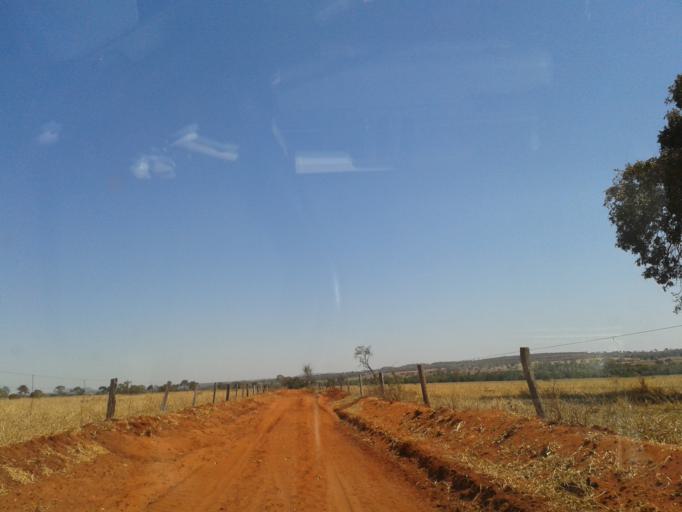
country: BR
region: Minas Gerais
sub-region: Santa Vitoria
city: Santa Vitoria
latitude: -19.0775
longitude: -50.0645
